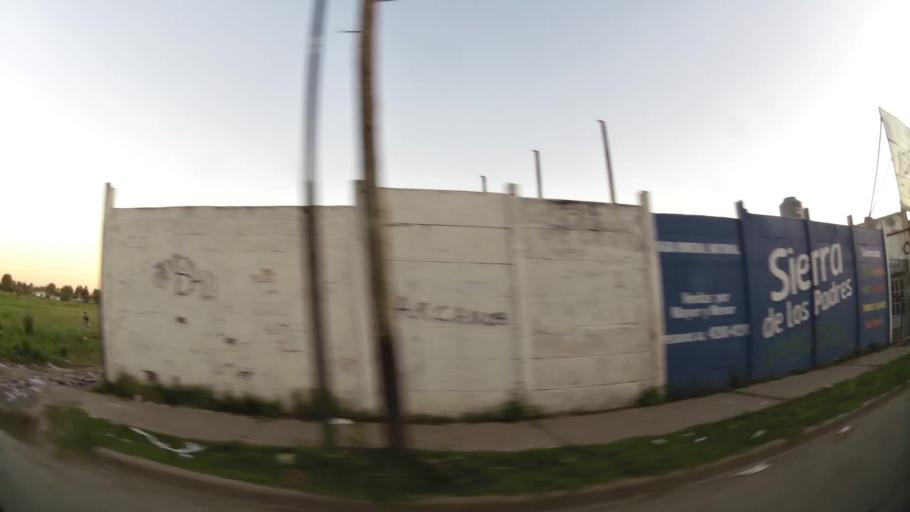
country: AR
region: Buenos Aires
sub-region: Partido de Almirante Brown
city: Adrogue
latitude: -34.8013
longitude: -58.3291
